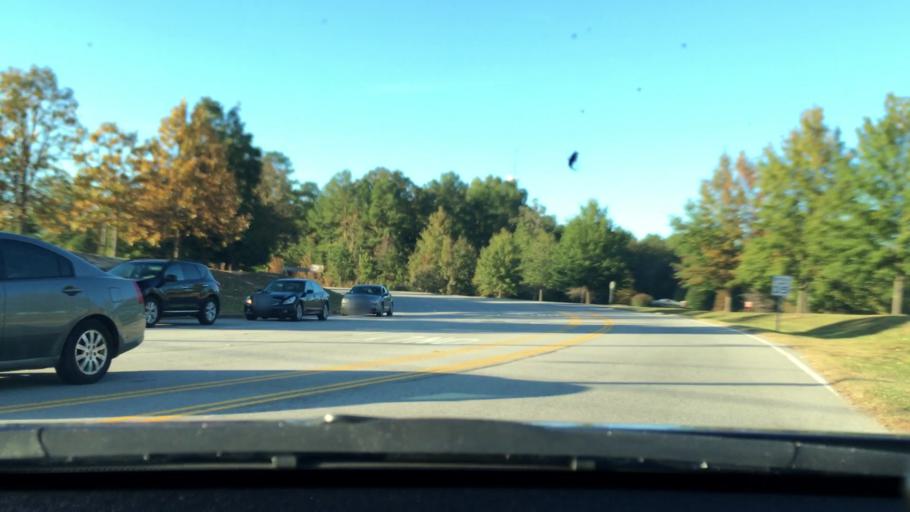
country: US
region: South Carolina
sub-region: Lexington County
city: Irmo
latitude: 34.0903
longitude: -81.1604
